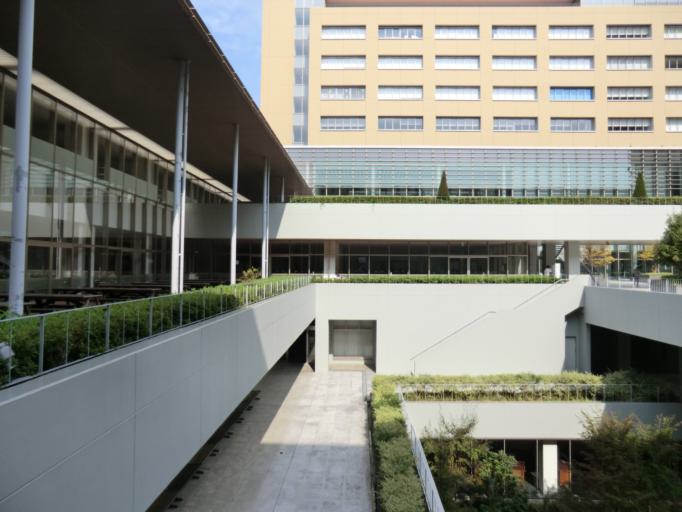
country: JP
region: Tokyo
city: Hino
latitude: 35.6445
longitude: 139.4071
